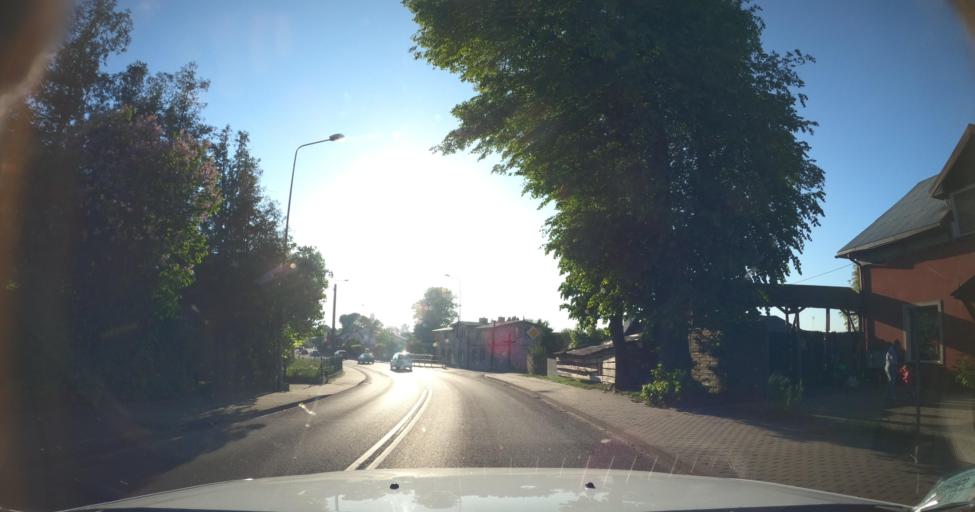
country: PL
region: Pomeranian Voivodeship
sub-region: Powiat kartuski
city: Przodkowo
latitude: 54.3156
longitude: 18.2713
